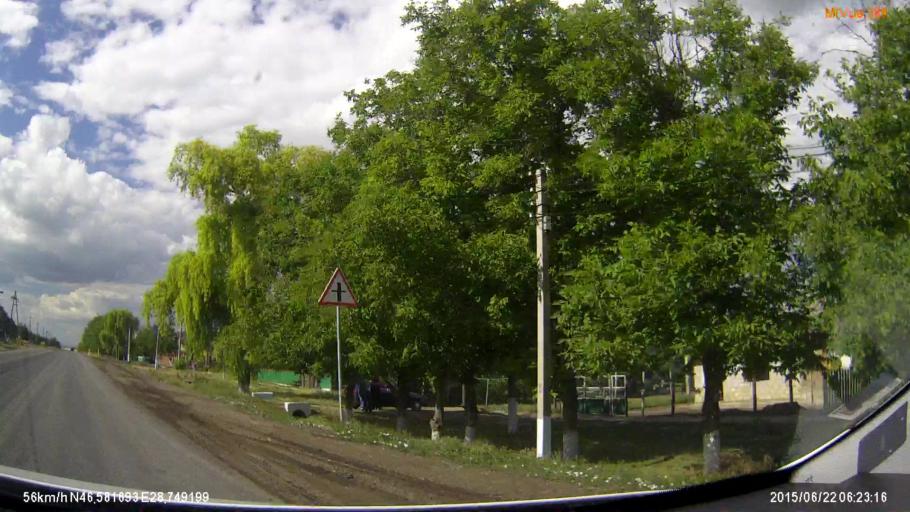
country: MD
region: Cimislia
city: Cimislia
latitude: 46.5814
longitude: 28.7493
